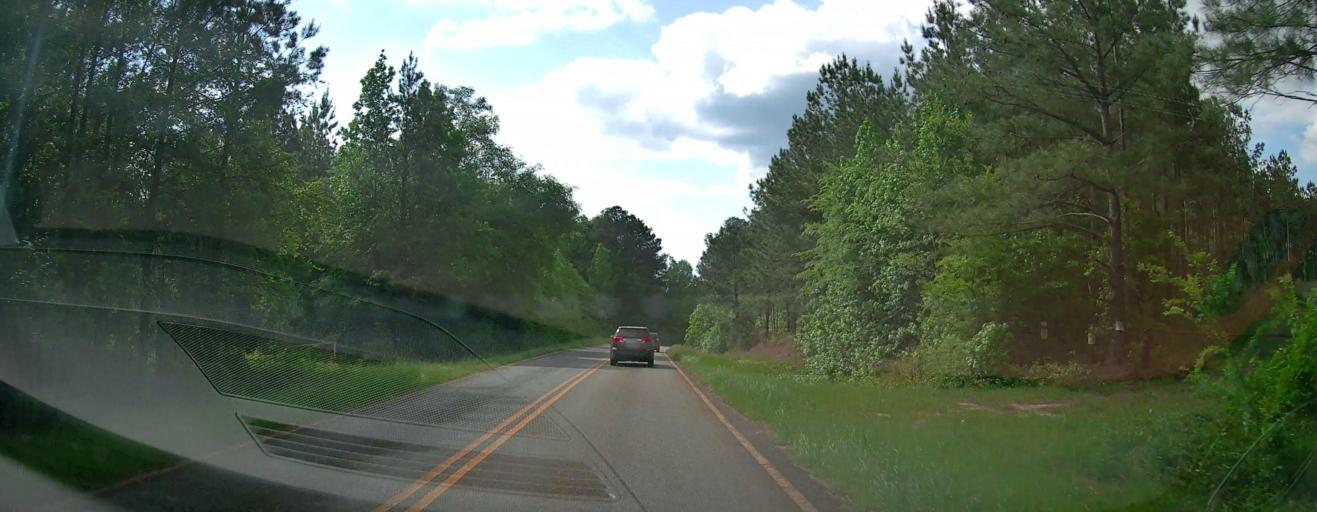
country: US
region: Georgia
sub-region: Laurens County
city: East Dublin
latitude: 32.7390
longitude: -82.9180
